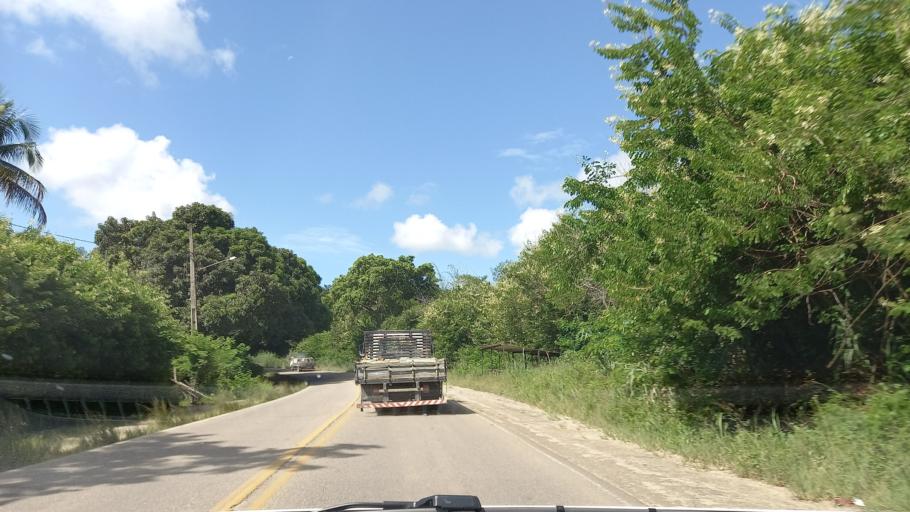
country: BR
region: Pernambuco
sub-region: Barreiros
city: Barreiros
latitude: -8.7950
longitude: -35.1888
